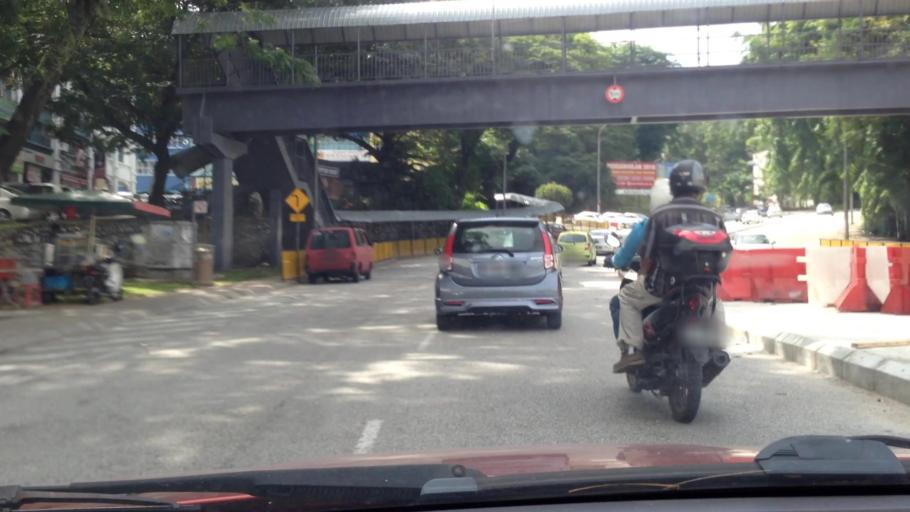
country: MY
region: Kuala Lumpur
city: Kuala Lumpur
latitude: 3.0914
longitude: 101.6762
